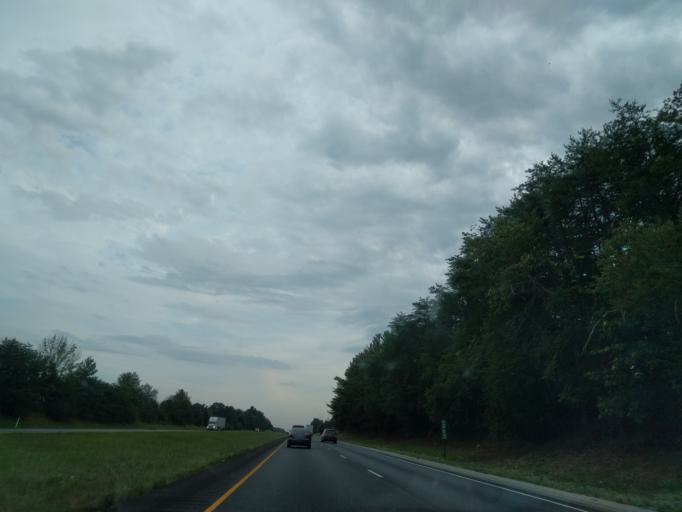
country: US
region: Indiana
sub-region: Scott County
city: Scottsburg
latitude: 38.6485
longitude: -85.7838
